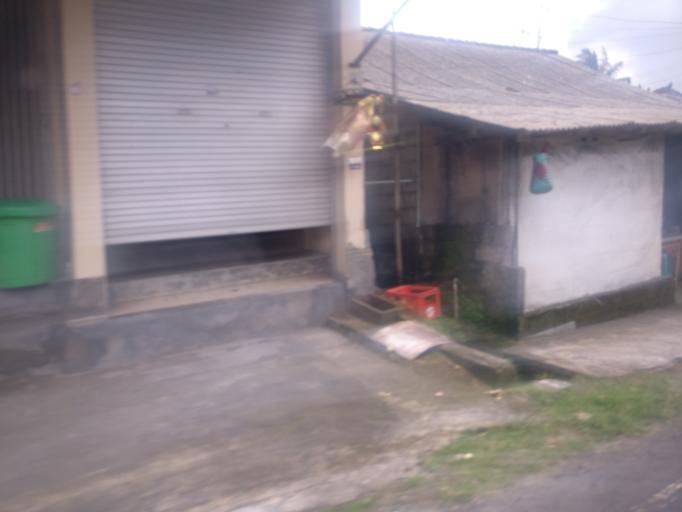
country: ID
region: Bali
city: Banjar Tengah
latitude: -8.4600
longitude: 115.2774
